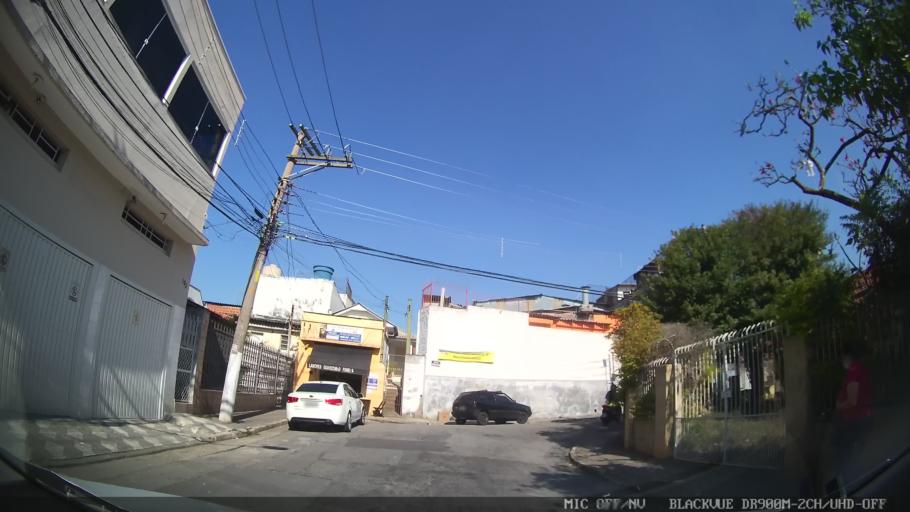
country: BR
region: Sao Paulo
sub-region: Sao Paulo
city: Sao Paulo
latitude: -23.5013
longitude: -46.6585
